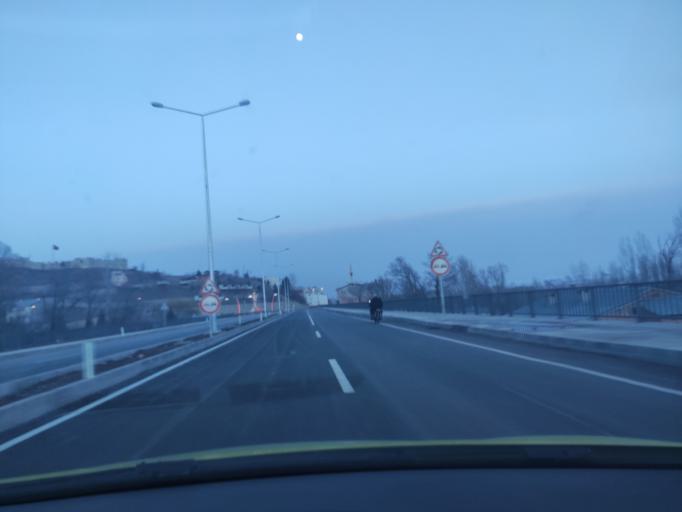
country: TR
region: Bayburt
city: Aydintepe
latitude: 40.3888
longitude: 40.1450
